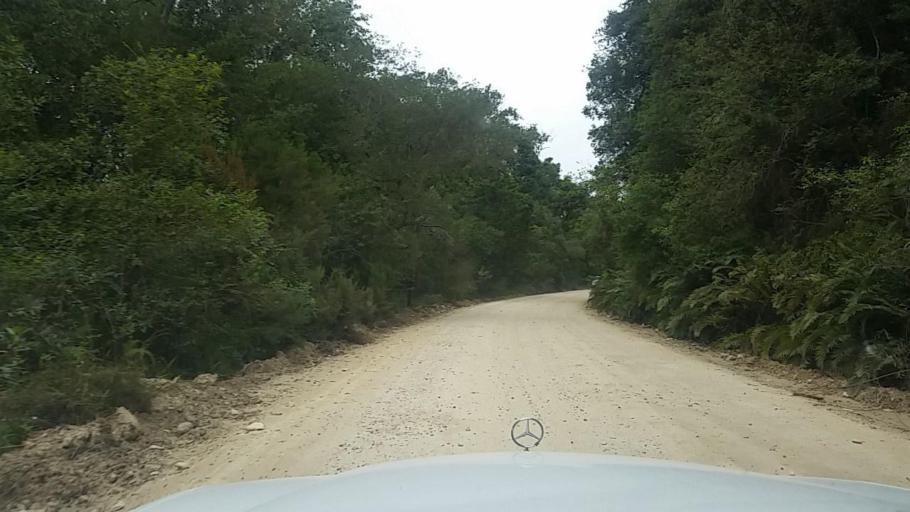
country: ZA
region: Western Cape
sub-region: Eden District Municipality
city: Knysna
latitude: -33.9688
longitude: 23.1488
